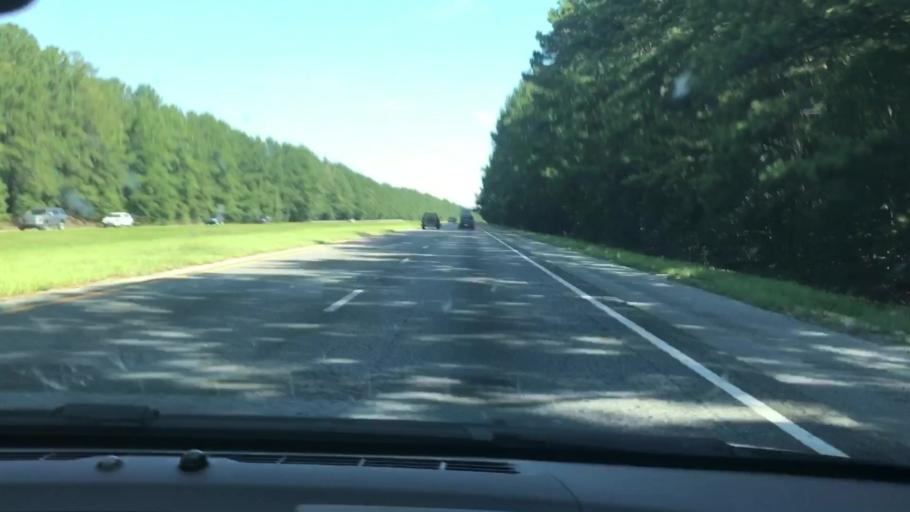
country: US
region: Alabama
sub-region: Russell County
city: Phenix City
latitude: 32.5891
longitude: -84.9586
